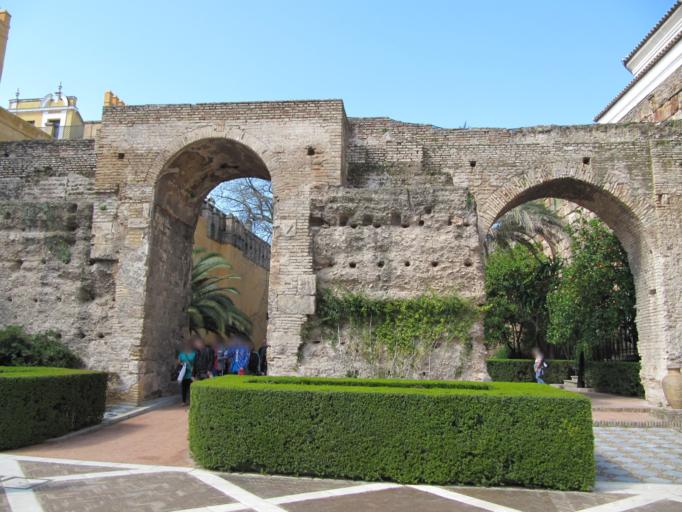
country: ES
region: Andalusia
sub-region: Provincia de Sevilla
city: Sevilla
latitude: 37.3840
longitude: -5.9917
